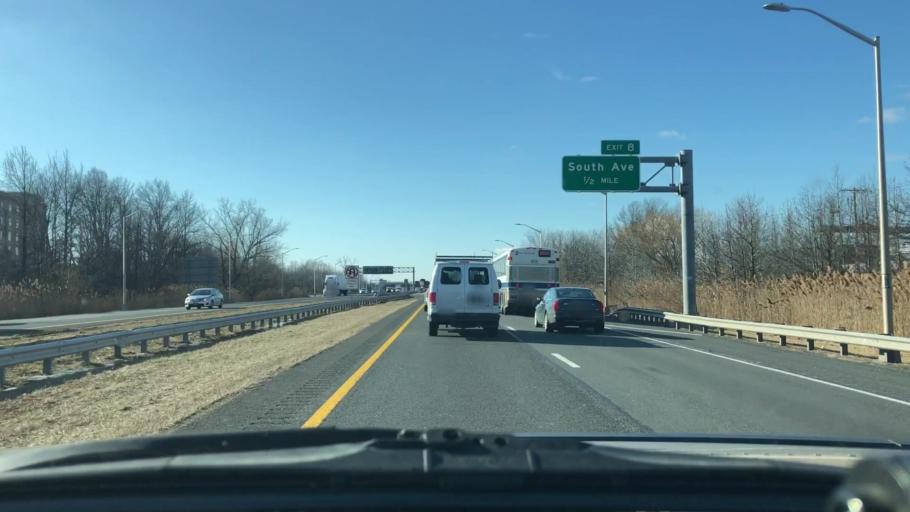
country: US
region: New York
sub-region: Richmond County
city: Bloomfield
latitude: 40.6147
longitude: -74.1790
